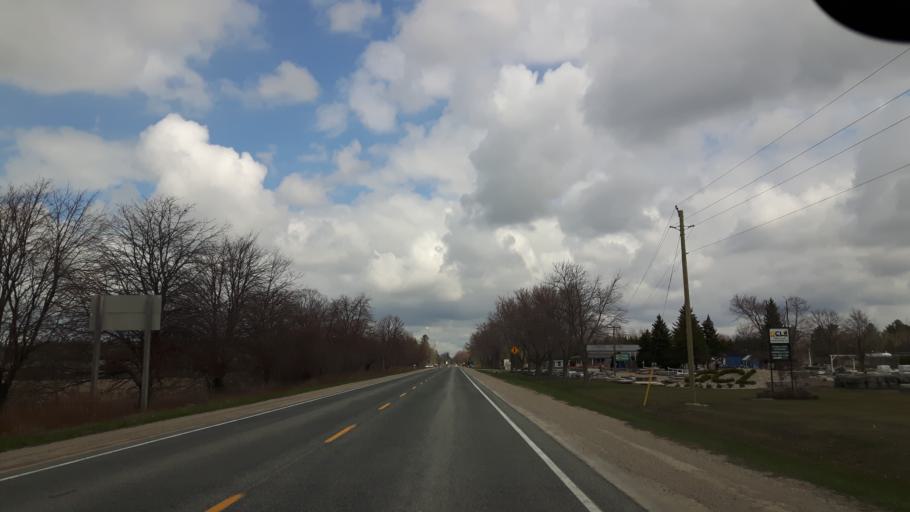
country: CA
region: Ontario
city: Bluewater
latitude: 43.5455
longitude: -81.6905
